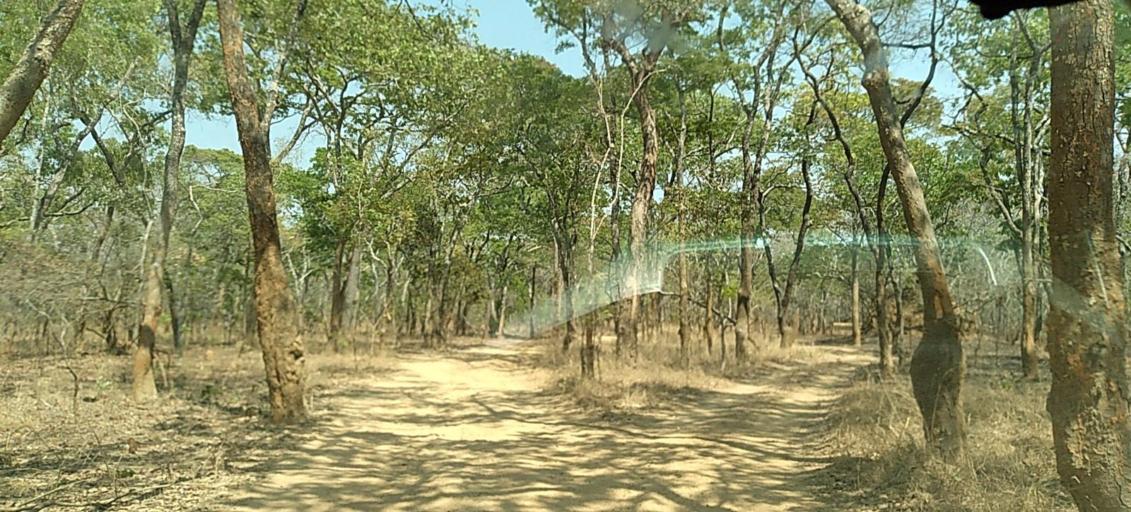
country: ZM
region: North-Western
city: Kasempa
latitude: -13.3927
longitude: 25.6225
